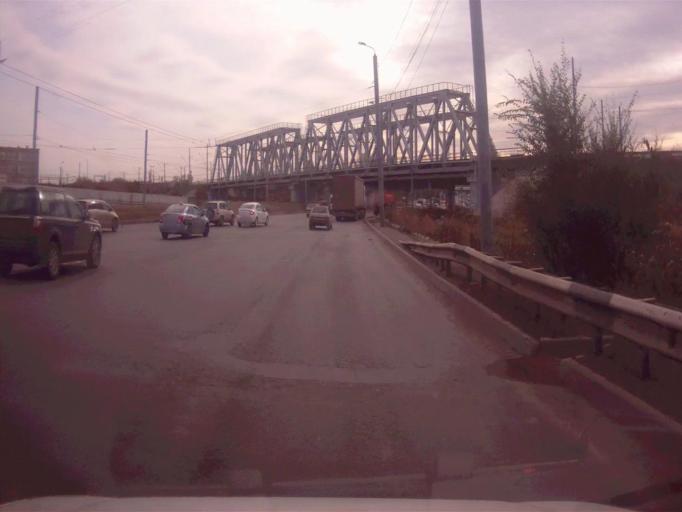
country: RU
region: Chelyabinsk
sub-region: Gorod Chelyabinsk
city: Chelyabinsk
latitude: 55.1554
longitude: 61.4429
